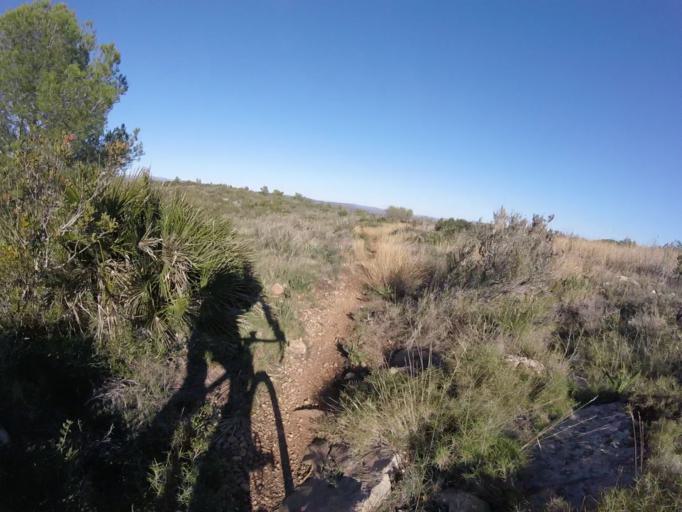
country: ES
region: Valencia
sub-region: Provincia de Castello
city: Orpesa/Oropesa del Mar
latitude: 40.1103
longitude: 0.1202
